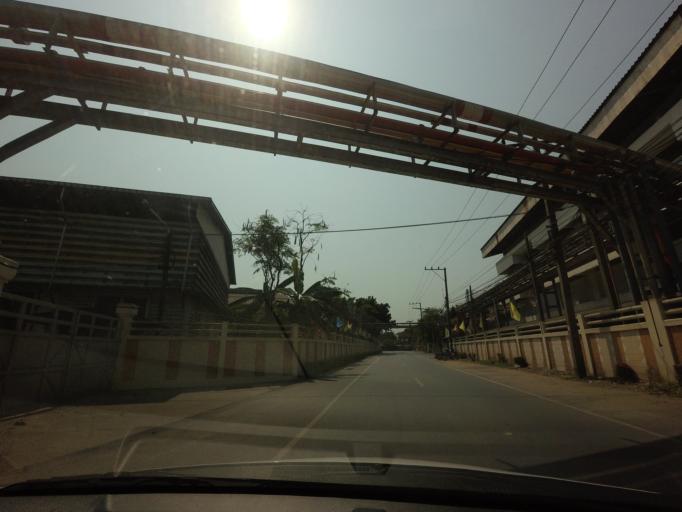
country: TH
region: Nakhon Pathom
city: Sam Phran
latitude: 13.7747
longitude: 100.2367
